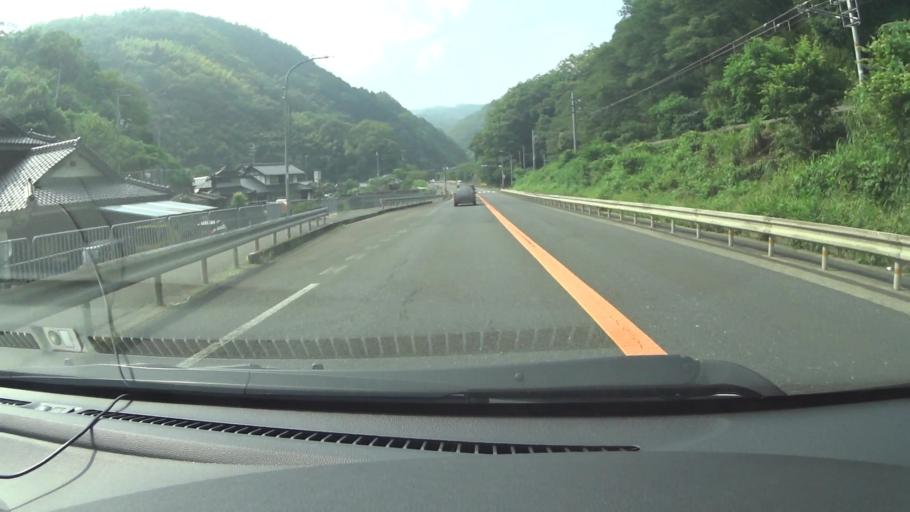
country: JP
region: Kyoto
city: Maizuru
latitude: 35.3803
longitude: 135.3157
